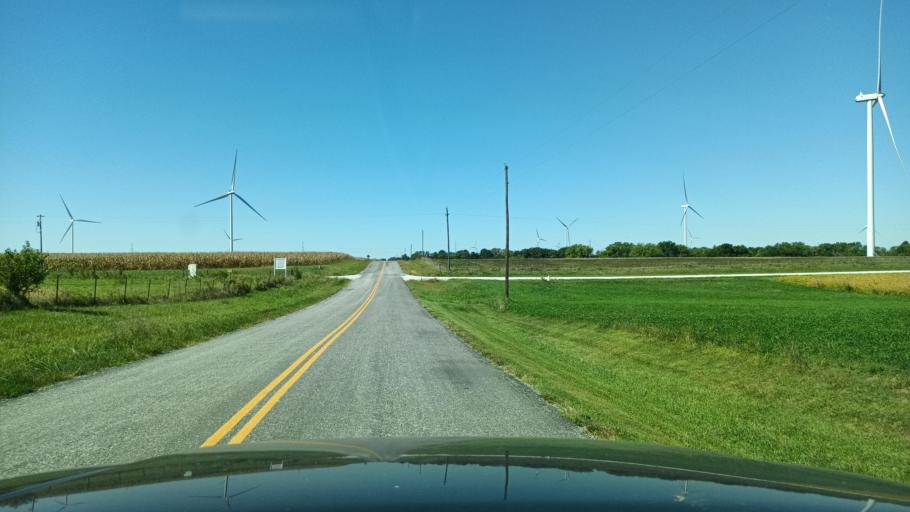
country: US
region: Missouri
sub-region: Adair County
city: Kirksville
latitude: 40.3307
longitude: -92.4780
